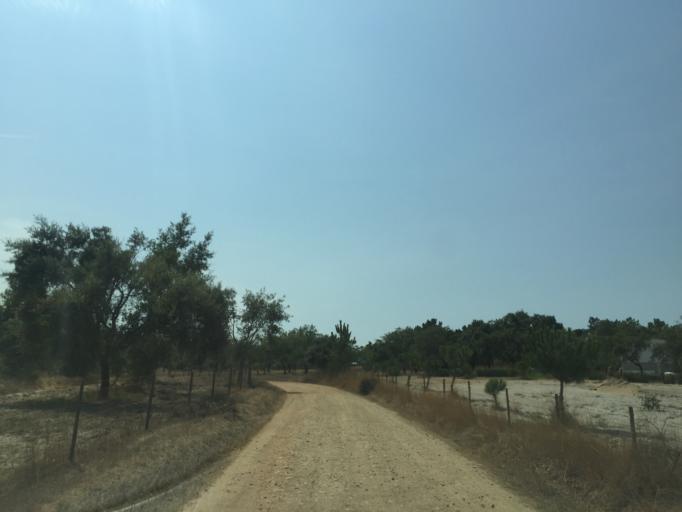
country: PT
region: Setubal
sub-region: Grandola
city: Grandola
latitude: 38.0039
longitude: -8.4953
